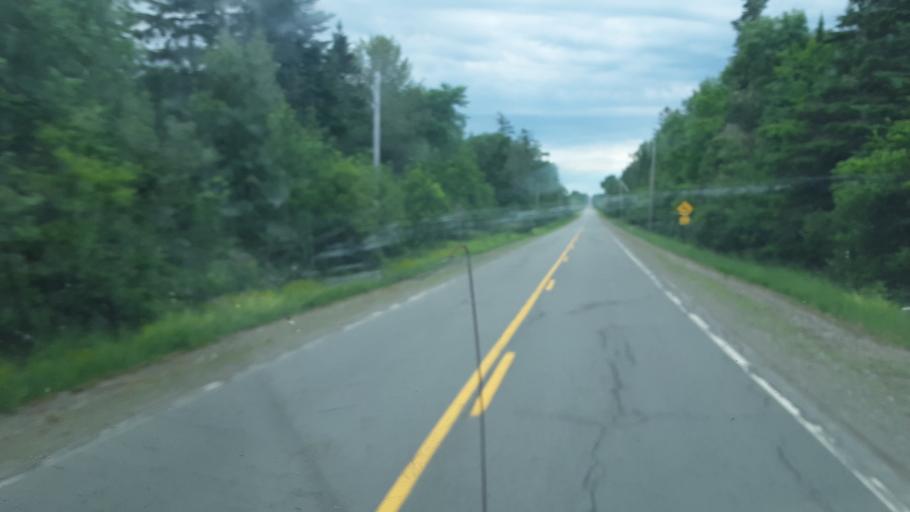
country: US
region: Maine
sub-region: Penobscot County
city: Patten
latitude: 45.8509
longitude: -68.3245
